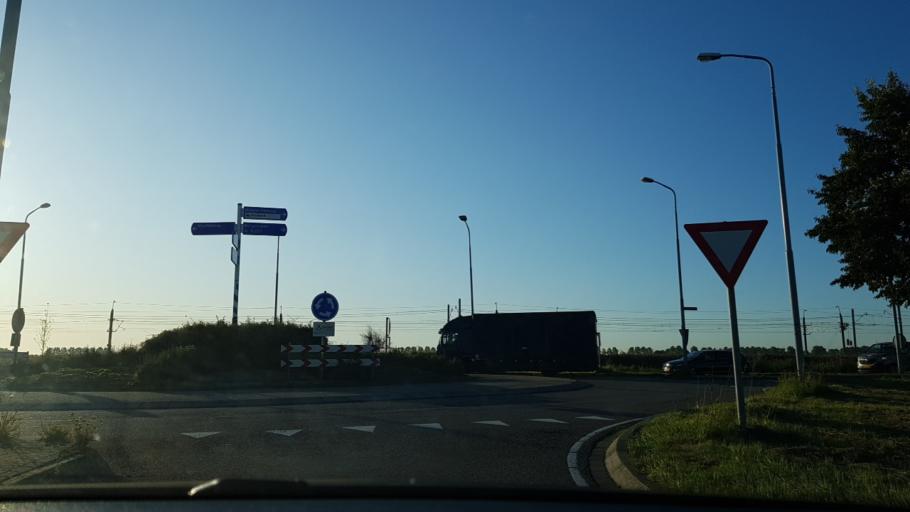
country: NL
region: South Holland
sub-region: Gemeente Kaag en Braassem
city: Leimuiden
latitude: 52.2674
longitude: 4.6556
